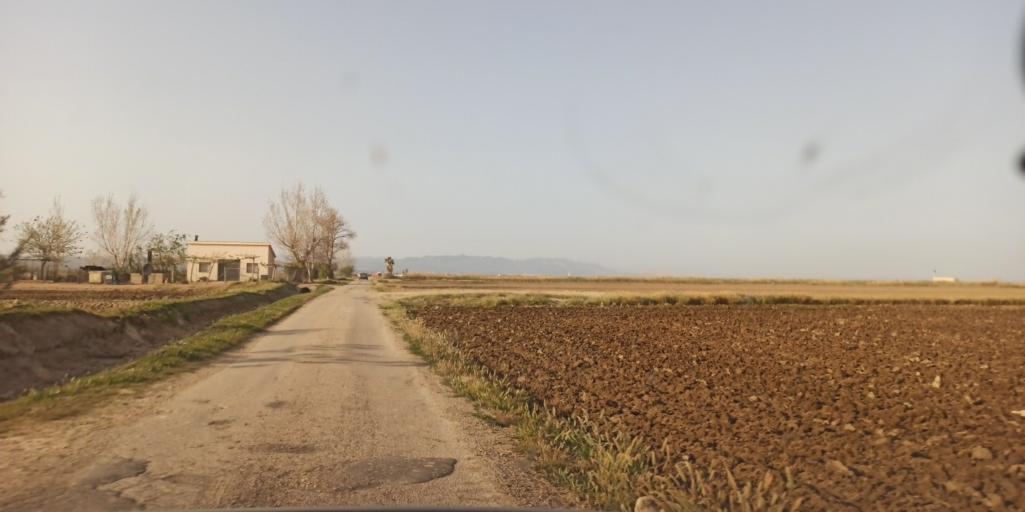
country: ES
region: Catalonia
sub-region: Provincia de Tarragona
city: Deltebre
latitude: 40.7597
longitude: 0.7542
